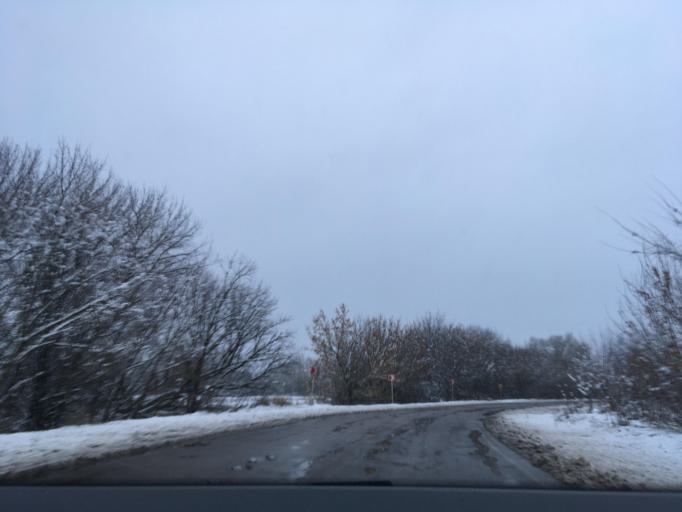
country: RU
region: Voronezj
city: Mitrofanovka
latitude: 50.1320
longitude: 39.9952
